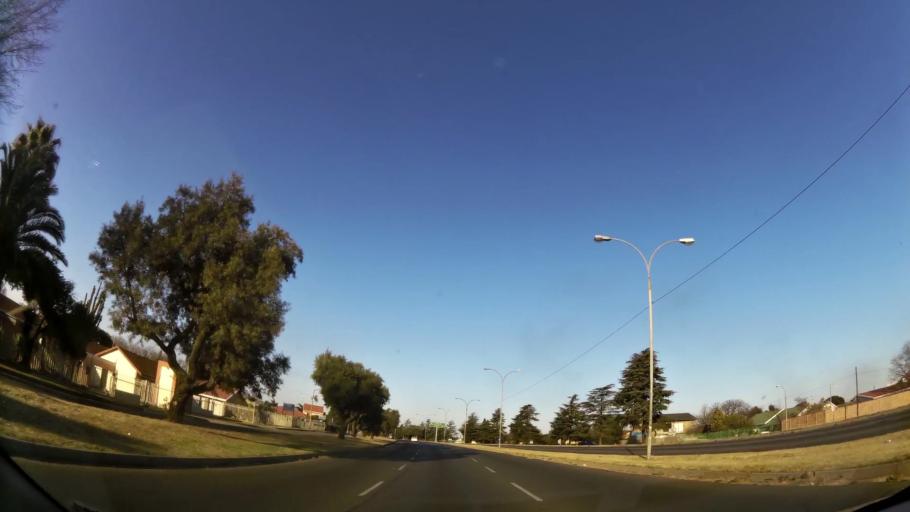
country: ZA
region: Gauteng
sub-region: City of Johannesburg Metropolitan Municipality
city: Roodepoort
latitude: -26.1472
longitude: 27.8877
